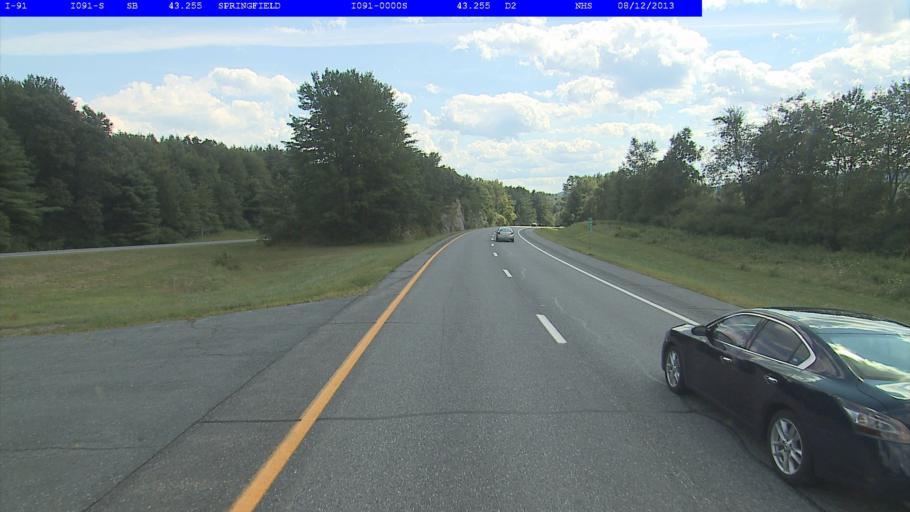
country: US
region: New Hampshire
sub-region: Sullivan County
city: Charlestown
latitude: 43.2880
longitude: -72.4278
